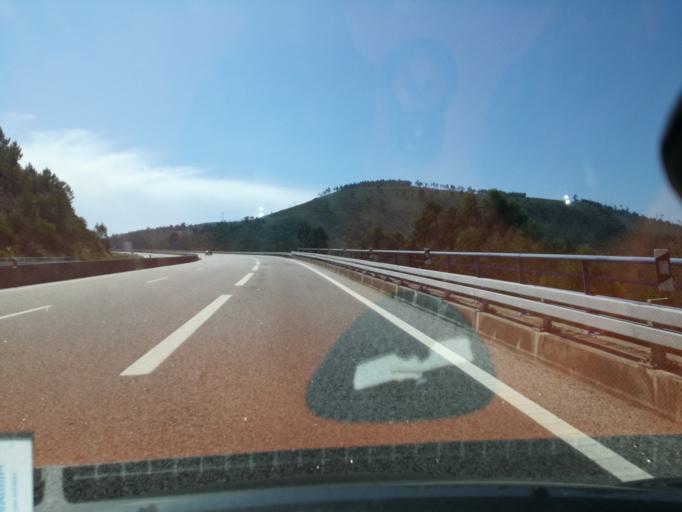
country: PT
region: Viana do Castelo
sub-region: Vila Nova de Cerveira
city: Vila Nova de Cerveira
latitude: 41.8641
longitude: -8.7804
